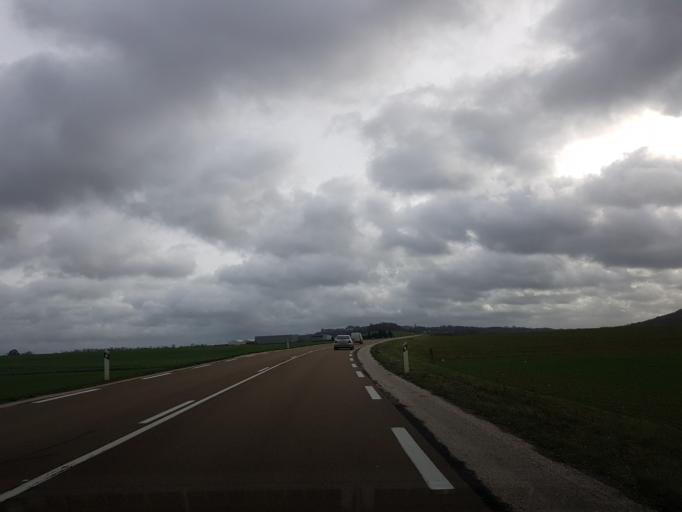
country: FR
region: Champagne-Ardenne
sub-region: Departement de la Haute-Marne
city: Langres
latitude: 47.8949
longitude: 5.3129
